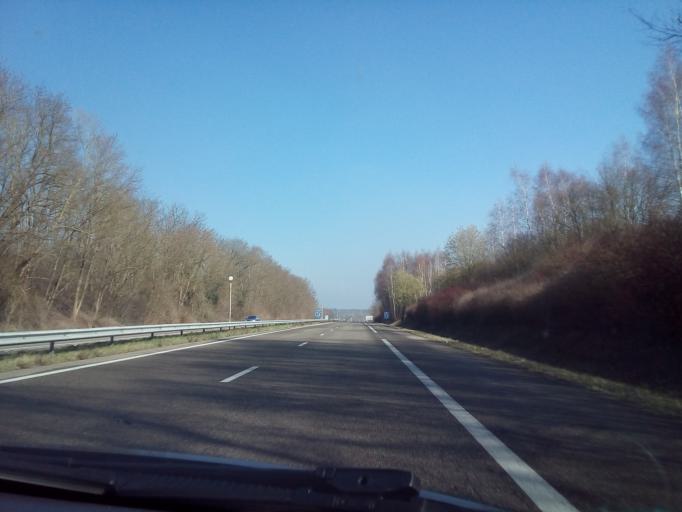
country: DE
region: Rheinland-Pfalz
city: Scheibenhardt
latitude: 48.9590
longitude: 8.1455
